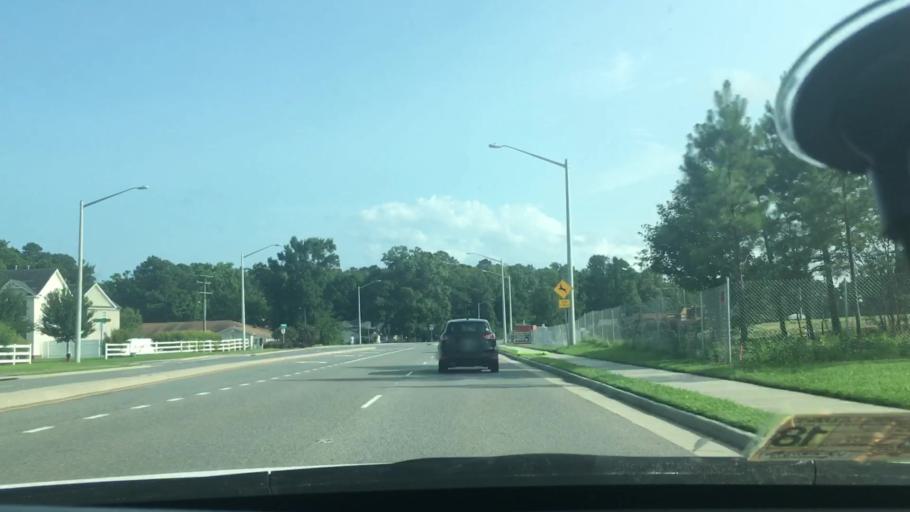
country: US
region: Virginia
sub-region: City of Virginia Beach
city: Virginia Beach
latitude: 36.8299
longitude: -75.9975
